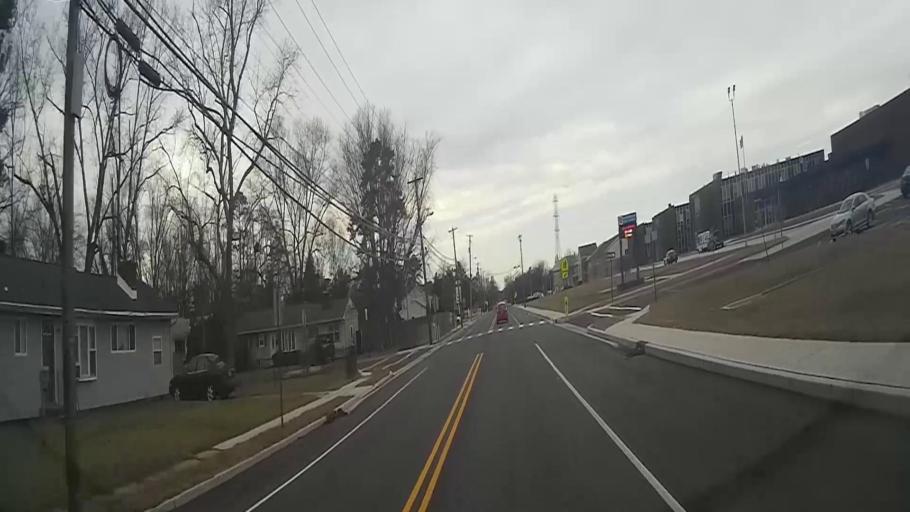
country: US
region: New Jersey
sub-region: Camden County
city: Pine Hill
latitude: 39.7765
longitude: -74.9650
